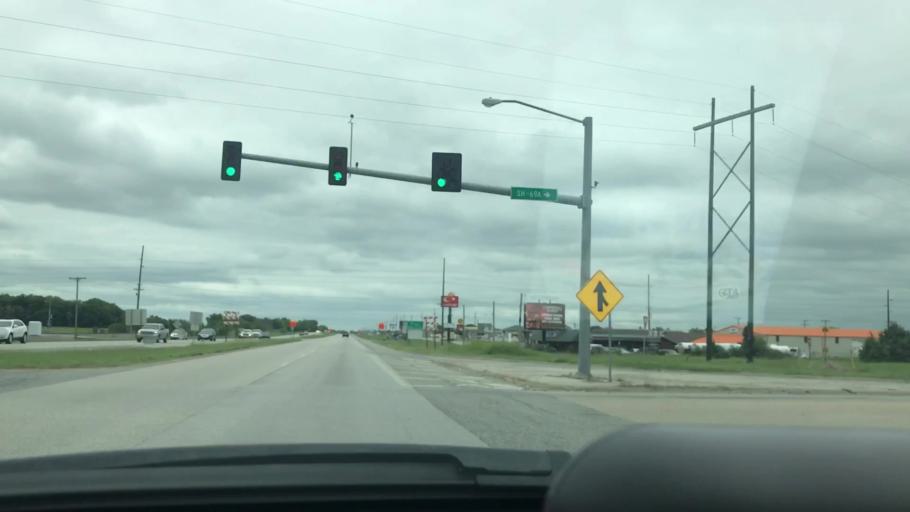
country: US
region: Oklahoma
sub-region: Mayes County
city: Chouteau
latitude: 36.2475
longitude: -95.3362
